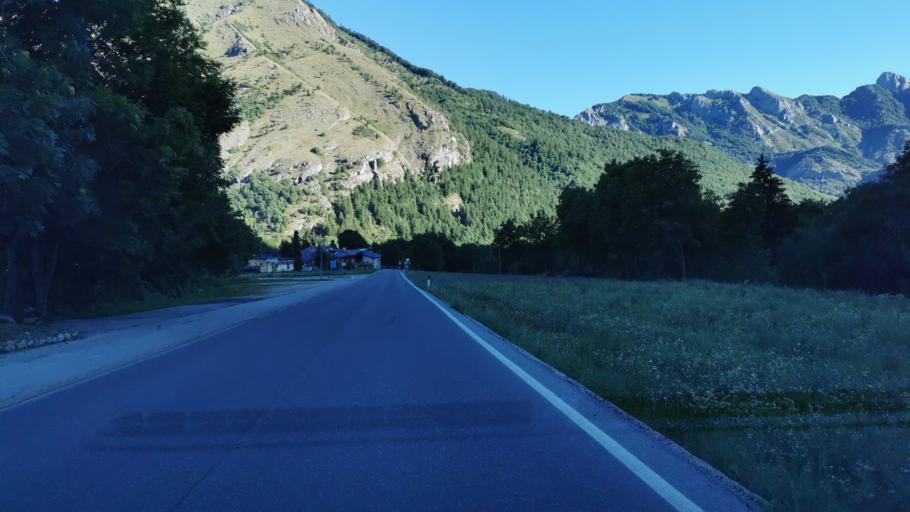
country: IT
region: Piedmont
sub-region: Provincia di Cuneo
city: Entracque
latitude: 44.2566
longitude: 7.3842
